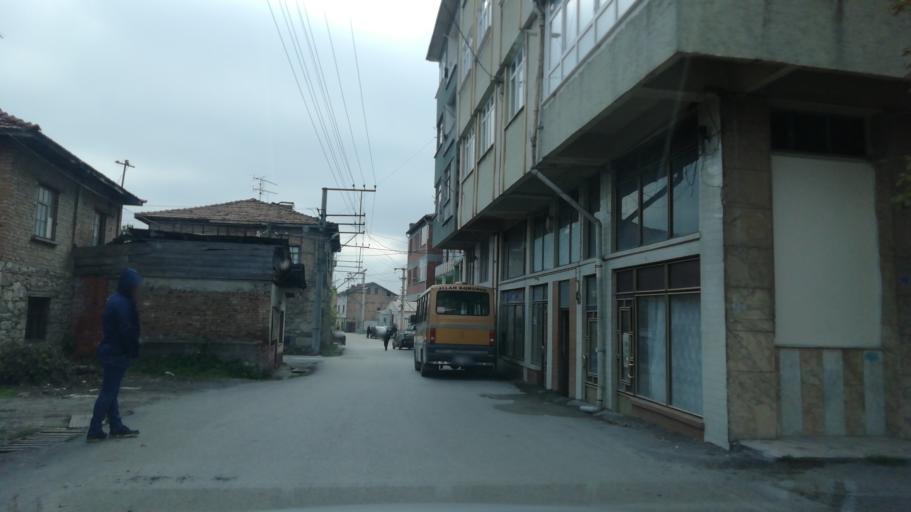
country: TR
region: Karabuk
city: Karabuk
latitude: 41.2209
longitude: 32.6276
